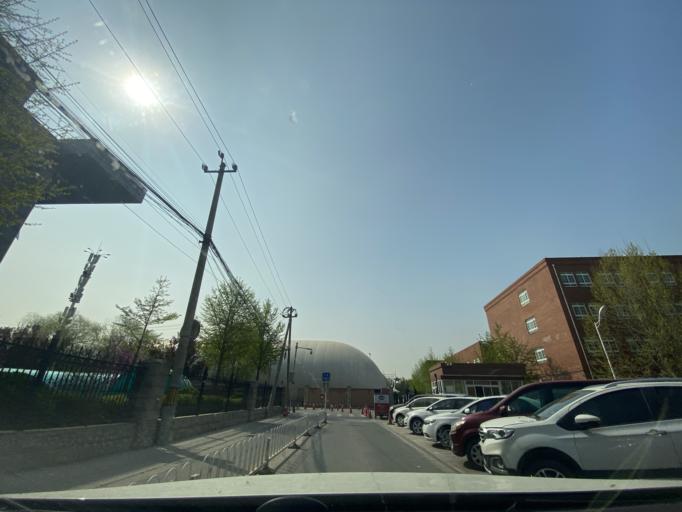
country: CN
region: Beijing
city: Sijiqing
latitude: 39.9428
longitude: 116.2510
